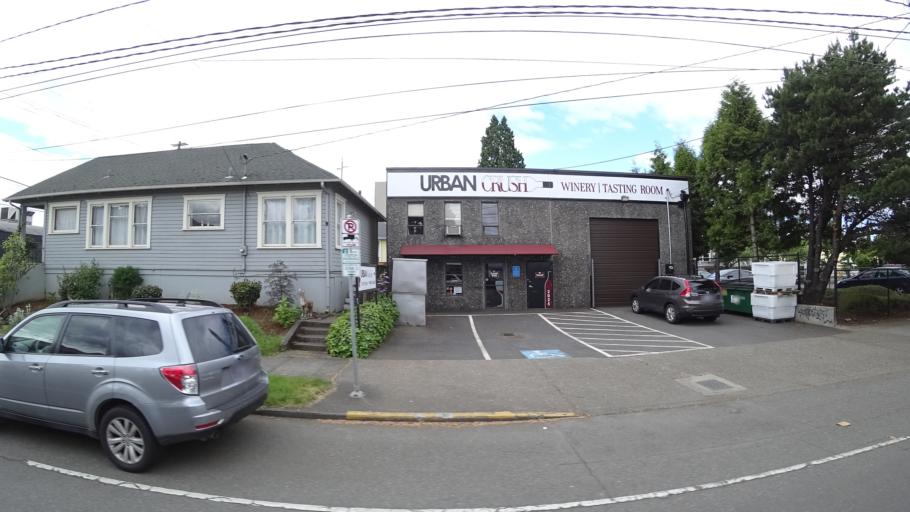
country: US
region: Oregon
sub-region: Multnomah County
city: Portland
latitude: 45.5082
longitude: -122.6588
